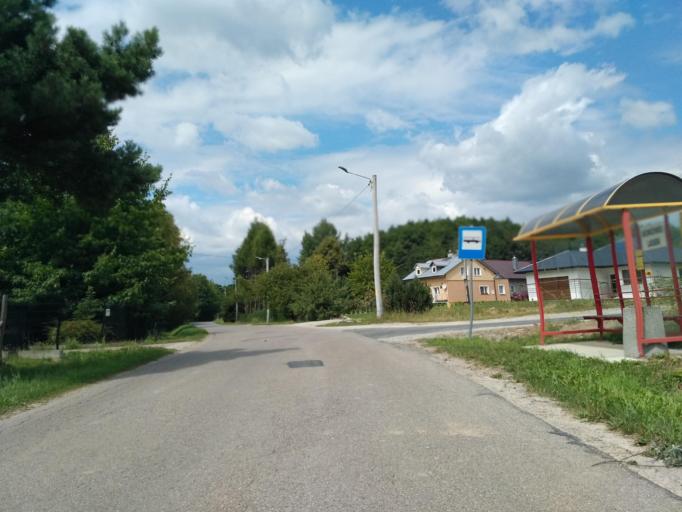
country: PL
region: Subcarpathian Voivodeship
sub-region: Powiat rzeszowski
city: Chmielnik
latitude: 49.9456
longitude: 22.1593
